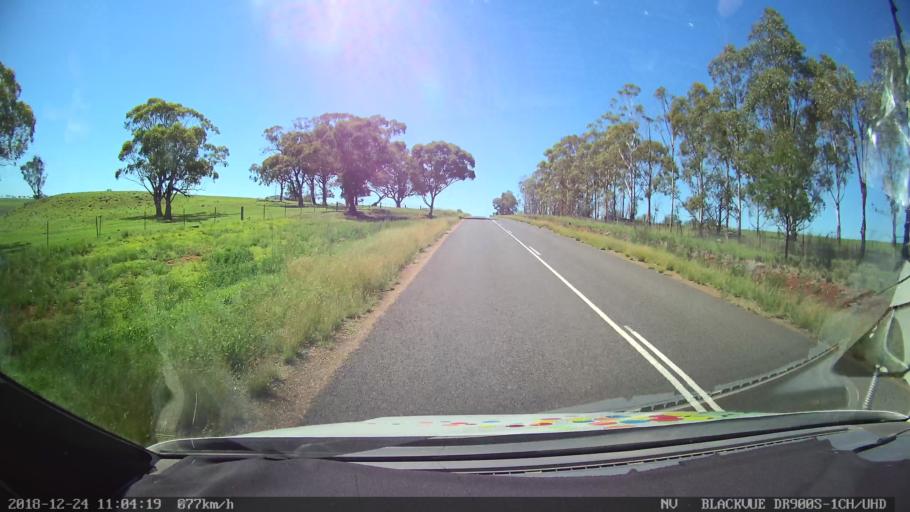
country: AU
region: New South Wales
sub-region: Upper Hunter Shire
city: Merriwa
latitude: -32.1075
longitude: 150.3717
